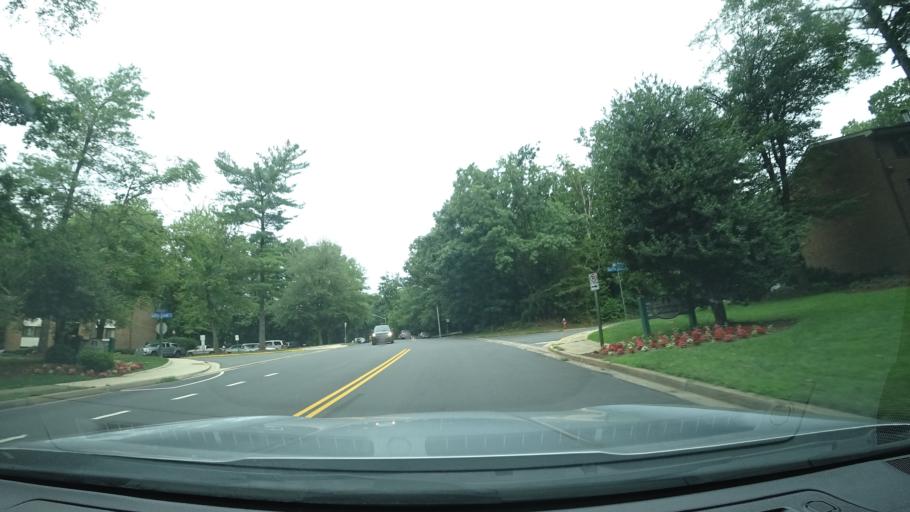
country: US
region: Virginia
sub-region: Fairfax County
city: Reston
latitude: 38.9701
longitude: -77.3354
